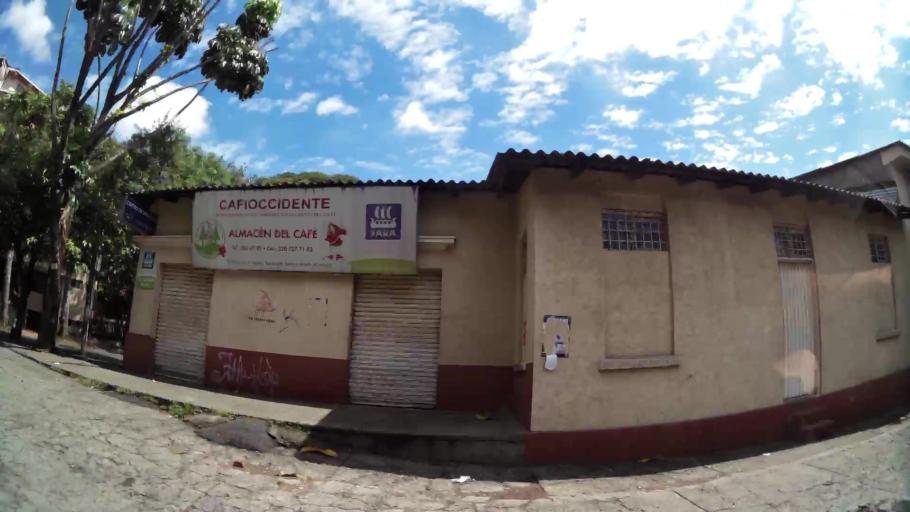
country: CO
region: Valle del Cauca
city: Cali
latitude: 3.4317
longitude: -76.5446
